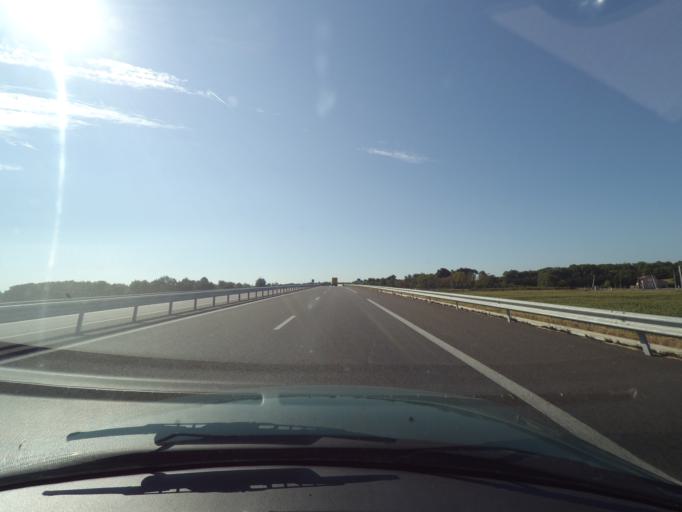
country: FR
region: Poitou-Charentes
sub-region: Departement de la Vienne
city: Terce
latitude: 46.4658
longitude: 0.5464
